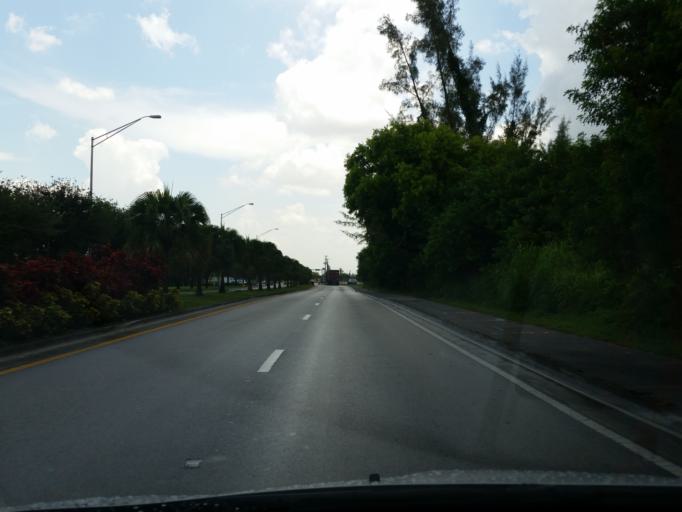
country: US
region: Florida
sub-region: Miami-Dade County
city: Sweetwater
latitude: 25.7836
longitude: -80.3751
